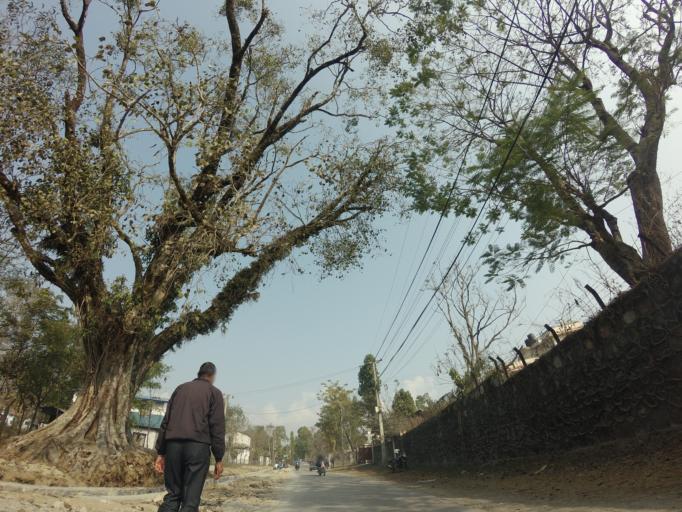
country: NP
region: Western Region
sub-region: Gandaki Zone
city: Pokhara
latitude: 28.2039
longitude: 83.9716
